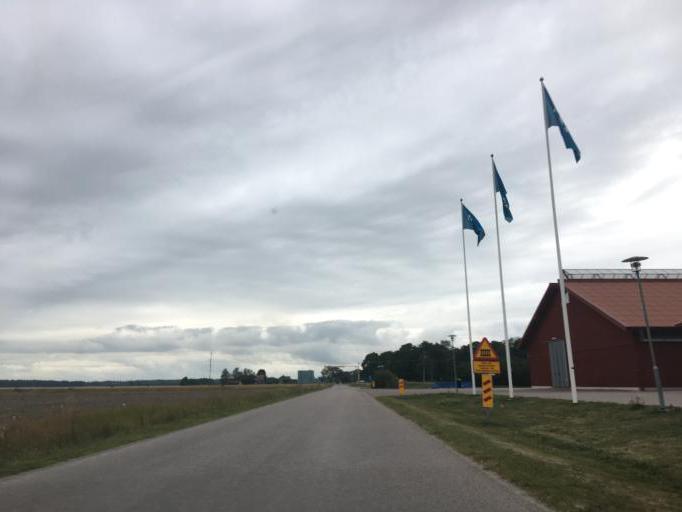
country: SE
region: Vaestmanland
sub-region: Hallstahammars Kommun
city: Kolback
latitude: 59.5201
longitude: 16.2487
